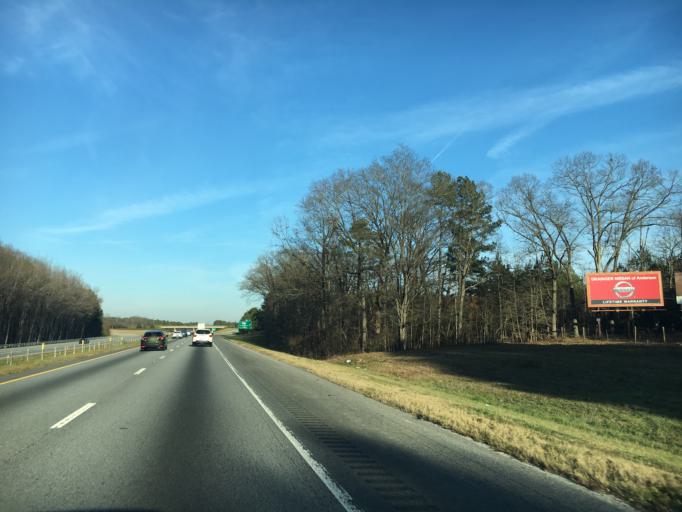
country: US
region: South Carolina
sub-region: Anderson County
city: Centerville
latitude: 34.5435
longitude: -82.8129
